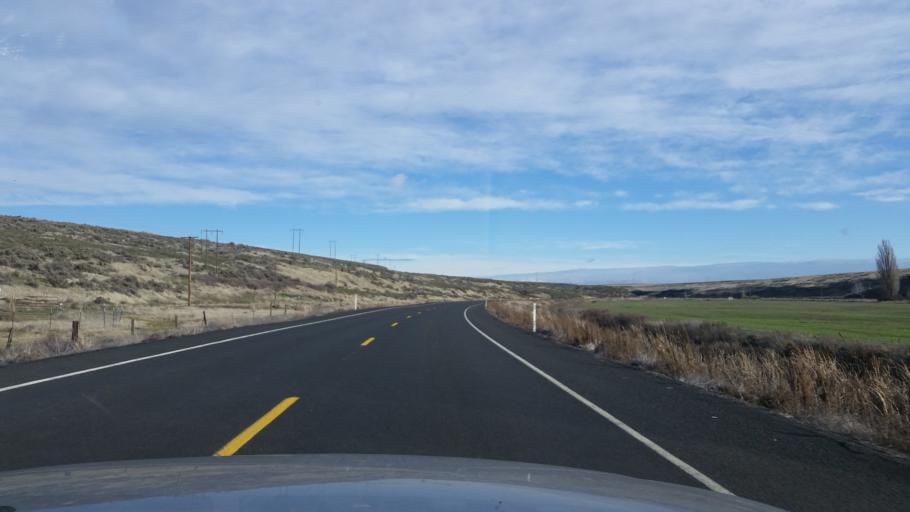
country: US
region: Washington
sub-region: Adams County
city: Ritzville
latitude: 47.3581
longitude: -118.5137
